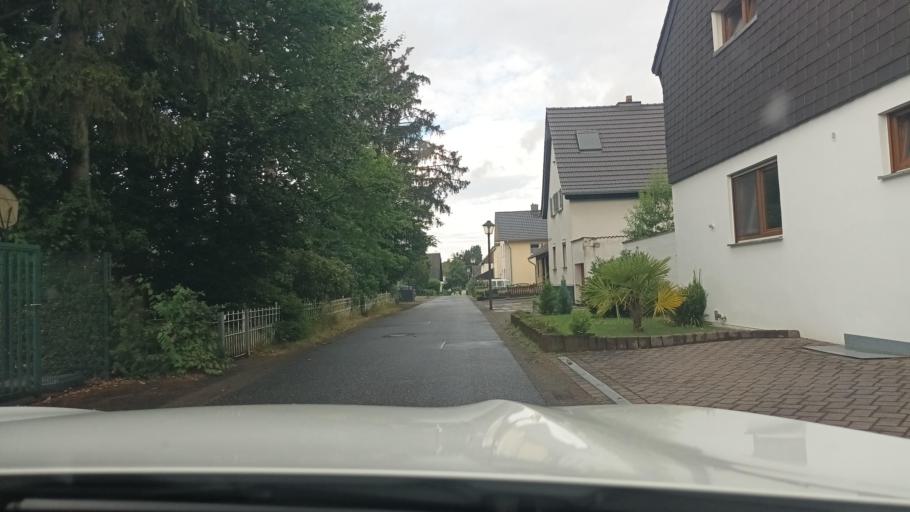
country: DE
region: North Rhine-Westphalia
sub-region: Regierungsbezirk Koln
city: Stossdorf
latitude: 50.7853
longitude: 7.2556
